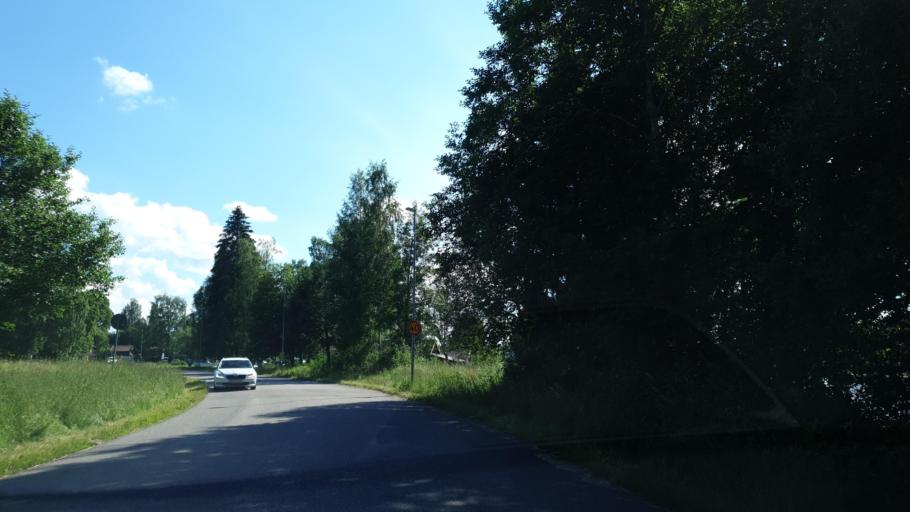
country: SE
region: Dalarna
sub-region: Avesta Kommun
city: Avesta
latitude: 60.1262
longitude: 16.2526
